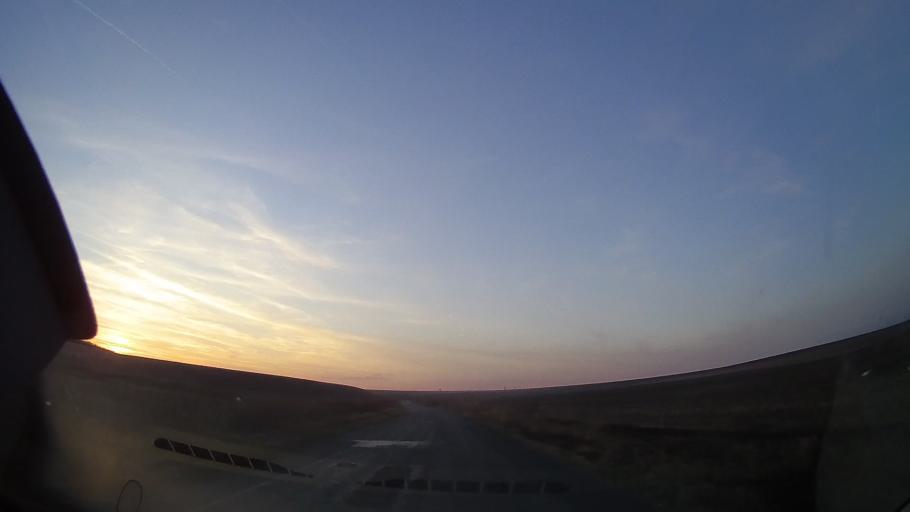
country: RO
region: Constanta
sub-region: Comuna Mereni
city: Mereni
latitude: 44.0185
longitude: 28.2980
